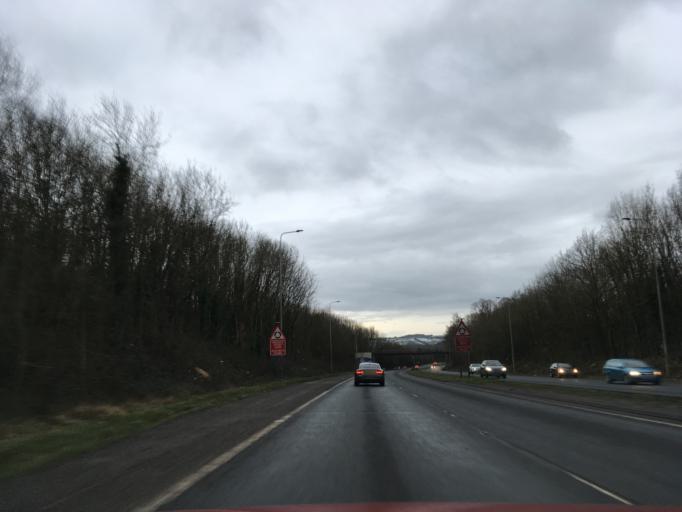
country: GB
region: Wales
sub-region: Rhondda Cynon Taf
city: Llantrisant
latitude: 51.5160
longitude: -3.3579
